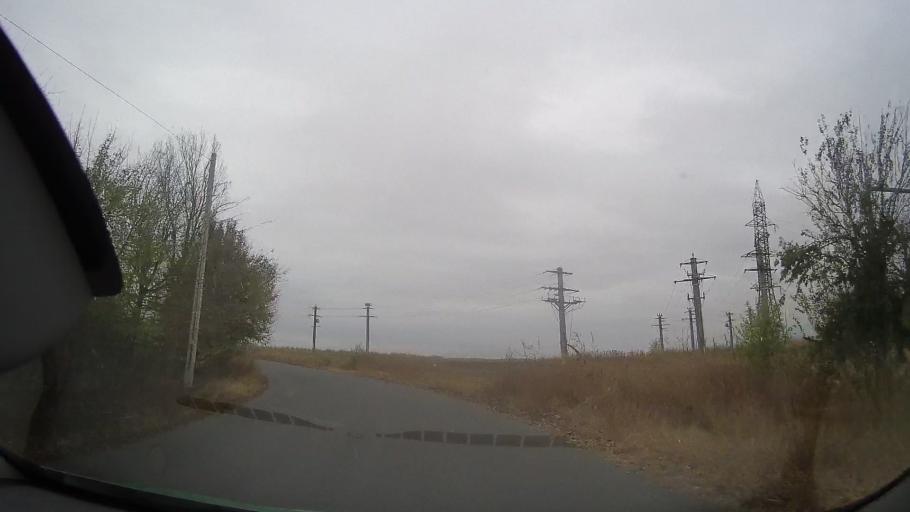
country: RO
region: Braila
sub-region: Comuna Rosiori
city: Rosiori
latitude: 44.8361
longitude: 27.3258
